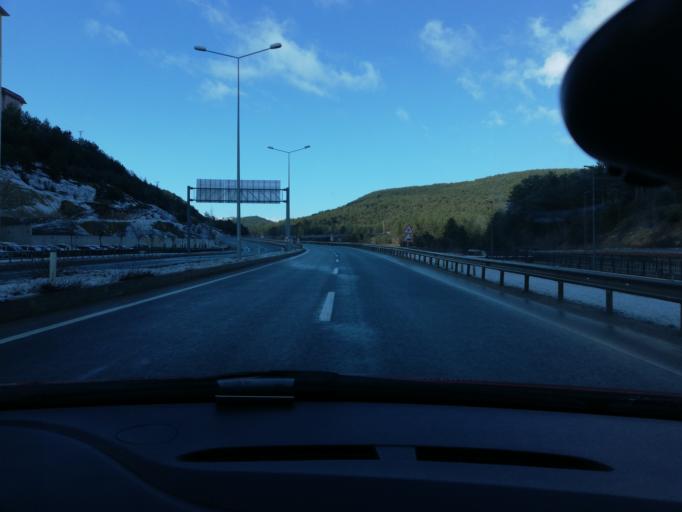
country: TR
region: Kastamonu
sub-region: Cide
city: Kastamonu
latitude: 41.3618
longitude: 33.7591
